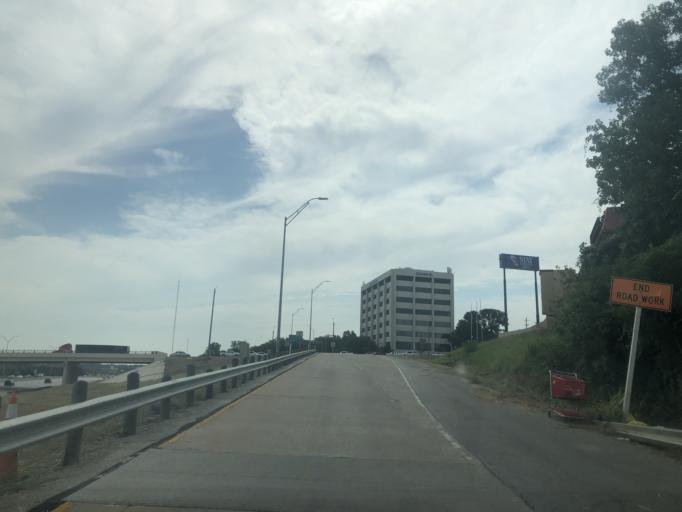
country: US
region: Texas
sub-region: Tarrant County
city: Fort Worth
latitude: 32.7489
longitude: -97.2914
